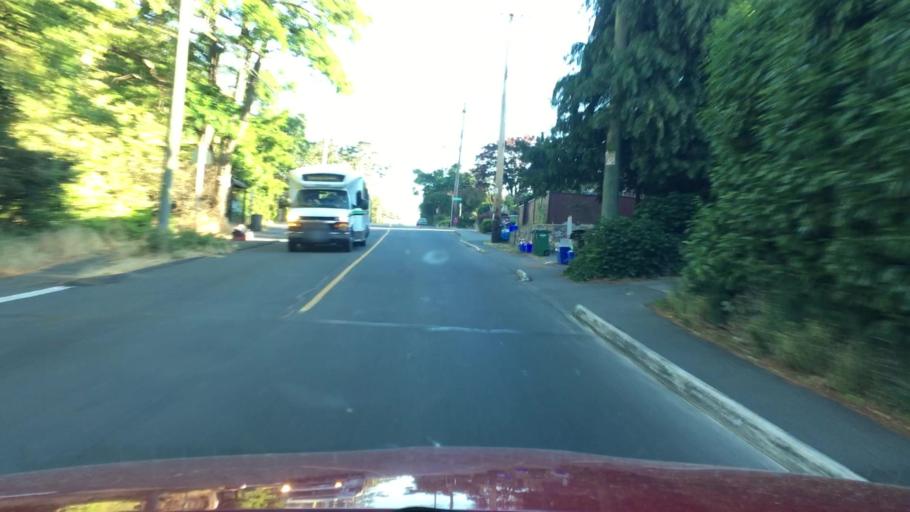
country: CA
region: British Columbia
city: Oak Bay
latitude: 48.4529
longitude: -123.3265
